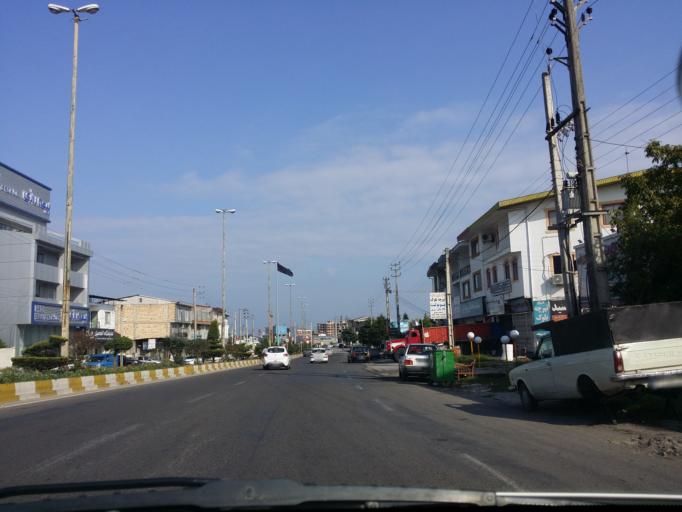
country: IR
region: Mazandaran
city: Chalus
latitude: 36.6794
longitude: 51.4029
